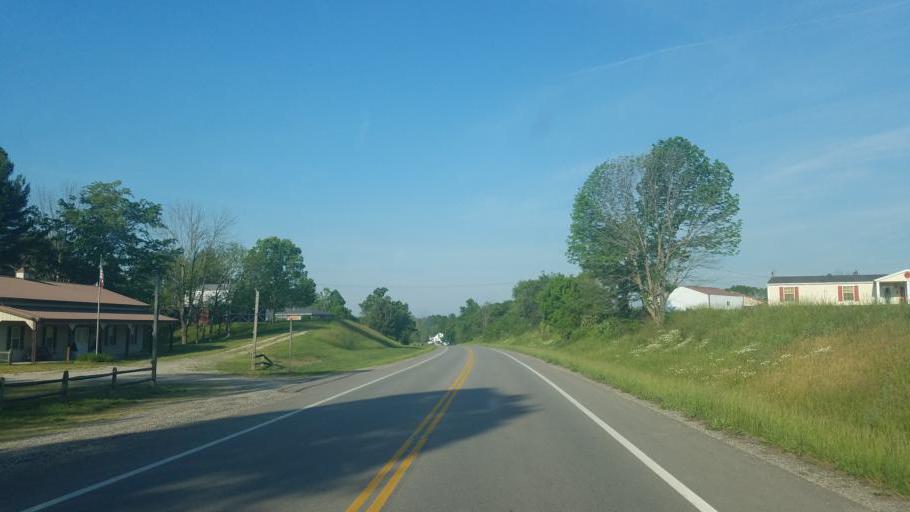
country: US
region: West Virginia
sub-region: Mason County
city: New Haven
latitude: 39.1334
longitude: -81.8692
